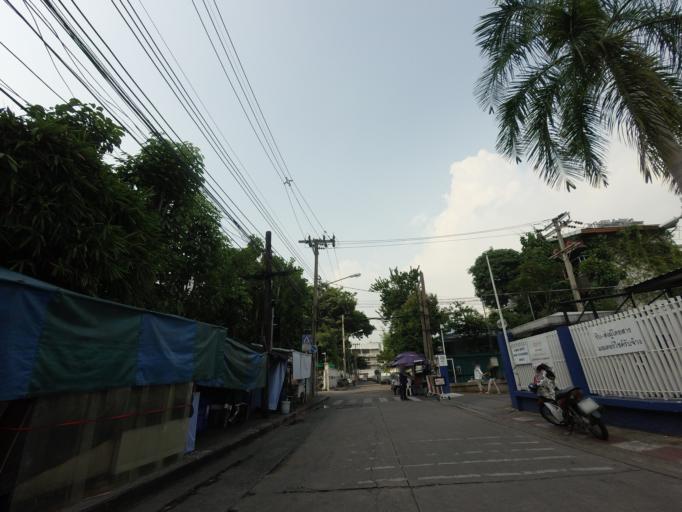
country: TH
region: Bangkok
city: Din Daeng
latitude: 13.7470
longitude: 100.5589
